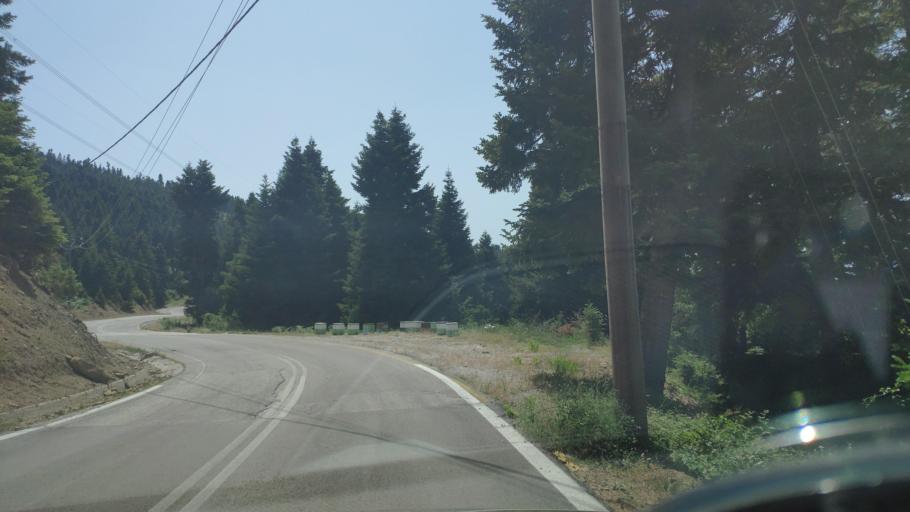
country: GR
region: Epirus
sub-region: Nomos Artas
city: Ano Kalentini
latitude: 39.2688
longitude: 21.2705
